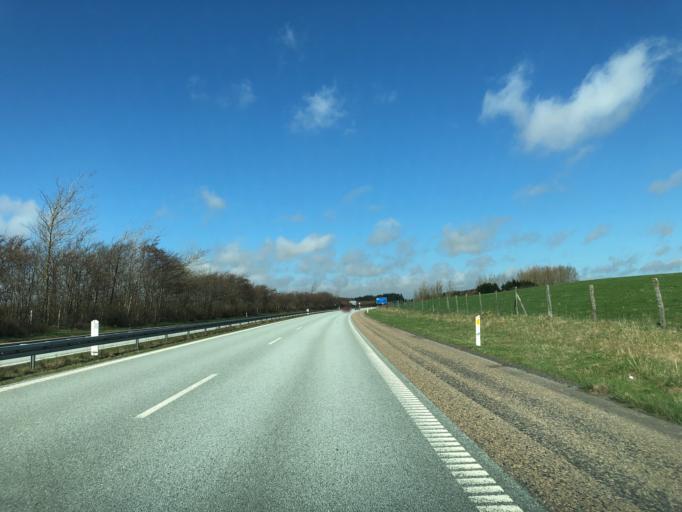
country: DK
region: North Denmark
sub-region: Hjorring Kommune
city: Hjorring
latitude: 57.5002
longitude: 10.0082
